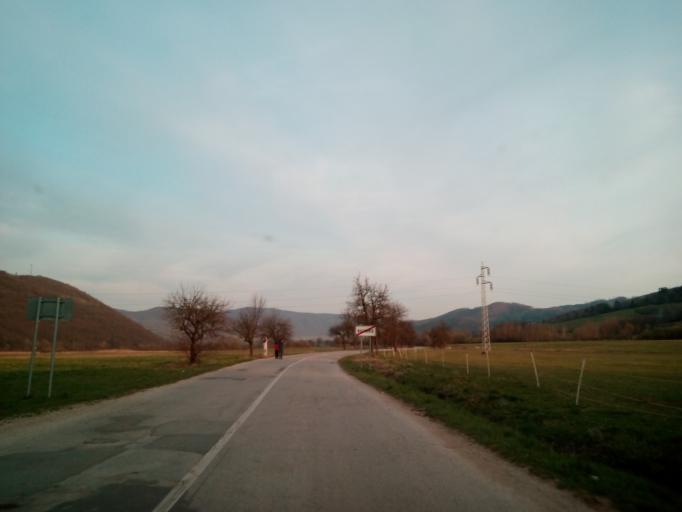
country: SK
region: Kosicky
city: Dobsina
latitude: 48.7008
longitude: 20.3035
